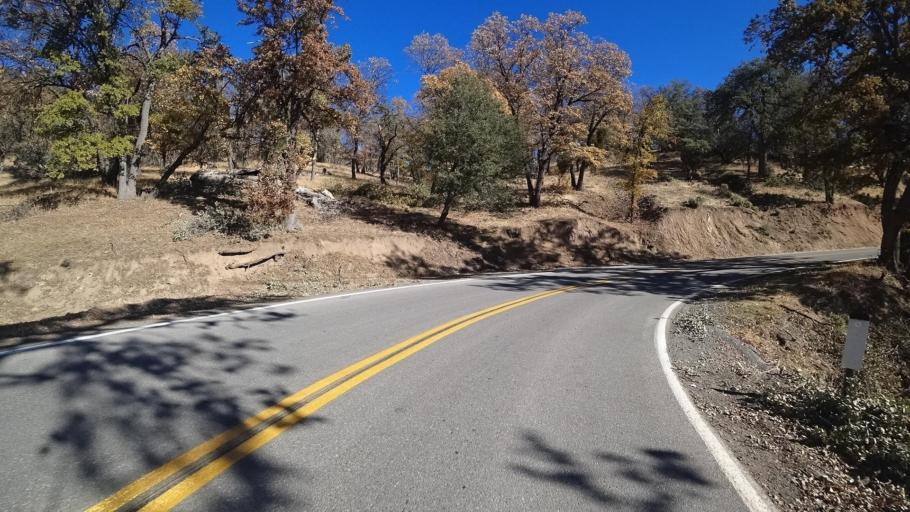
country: US
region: California
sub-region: Kern County
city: Alta Sierra
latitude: 35.7426
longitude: -118.6065
